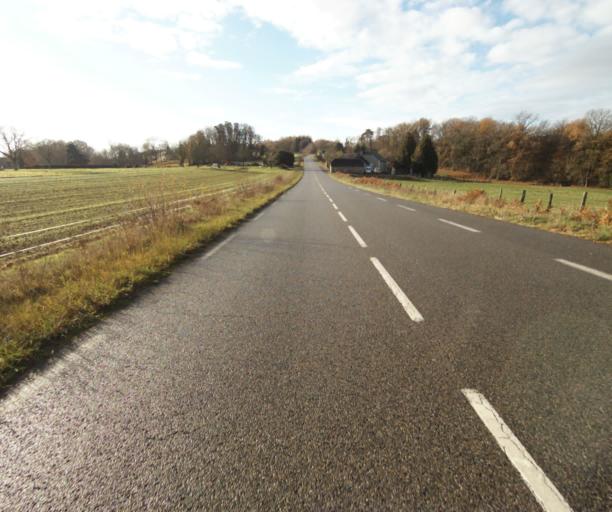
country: FR
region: Limousin
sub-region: Departement de la Correze
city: Saint-Mexant
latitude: 45.2553
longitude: 1.6337
